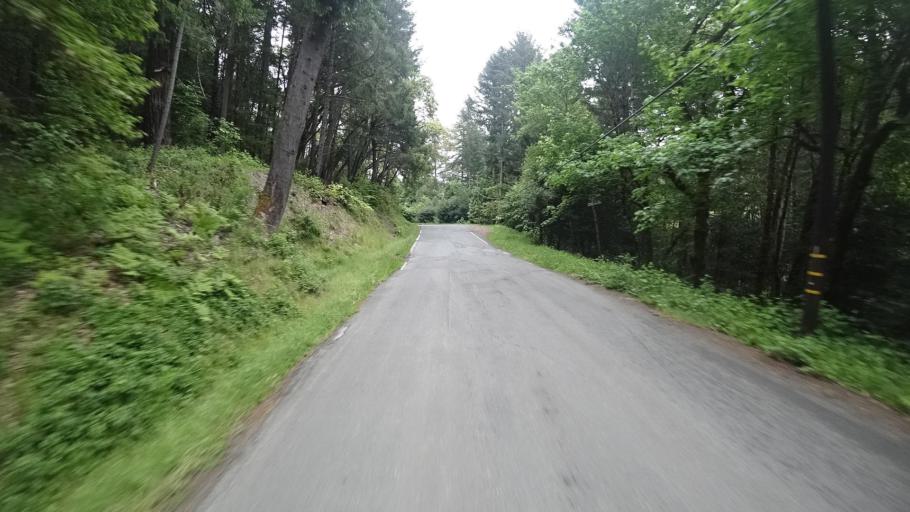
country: US
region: California
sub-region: Humboldt County
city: Willow Creek
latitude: 41.1976
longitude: -123.7409
